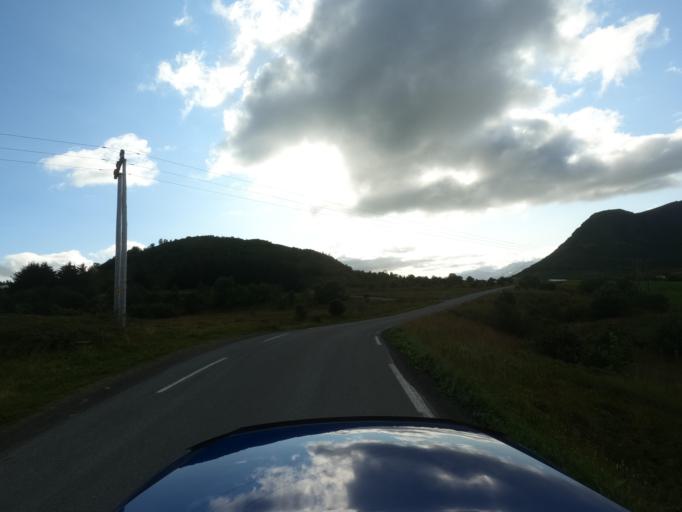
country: NO
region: Nordland
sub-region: Vestvagoy
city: Gravdal
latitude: 68.1713
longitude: 13.5599
